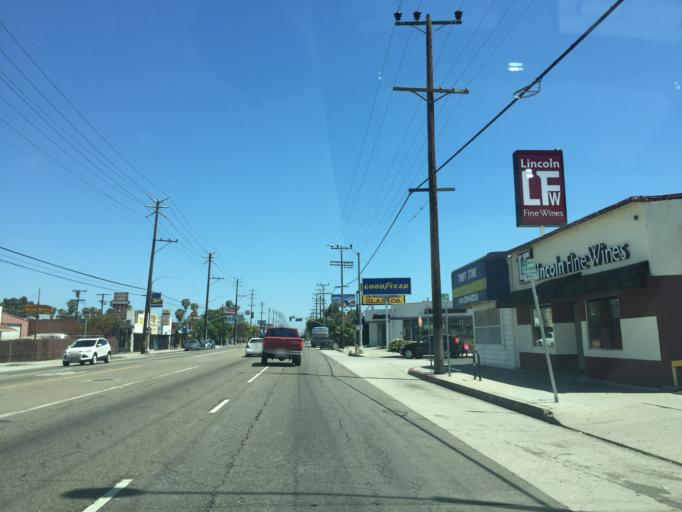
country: US
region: California
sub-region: Los Angeles County
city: Marina del Rey
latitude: 33.9994
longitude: -118.4641
